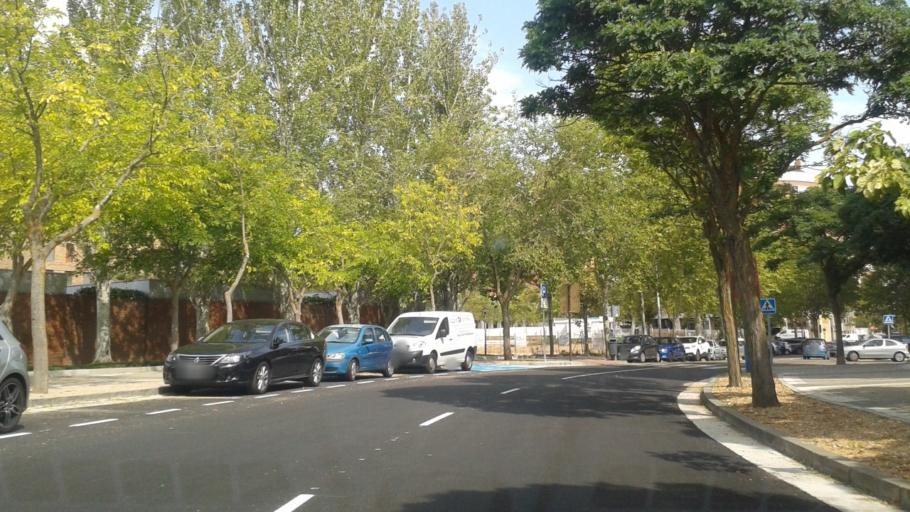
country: ES
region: Castille and Leon
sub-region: Provincia de Valladolid
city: Zaratan
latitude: 41.6339
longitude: -4.7608
